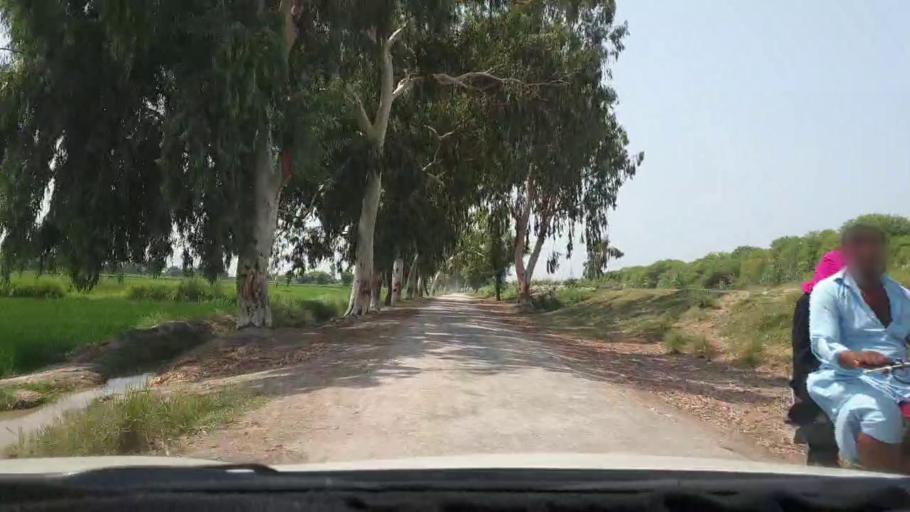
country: PK
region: Sindh
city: Dokri
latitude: 27.3168
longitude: 68.1049
